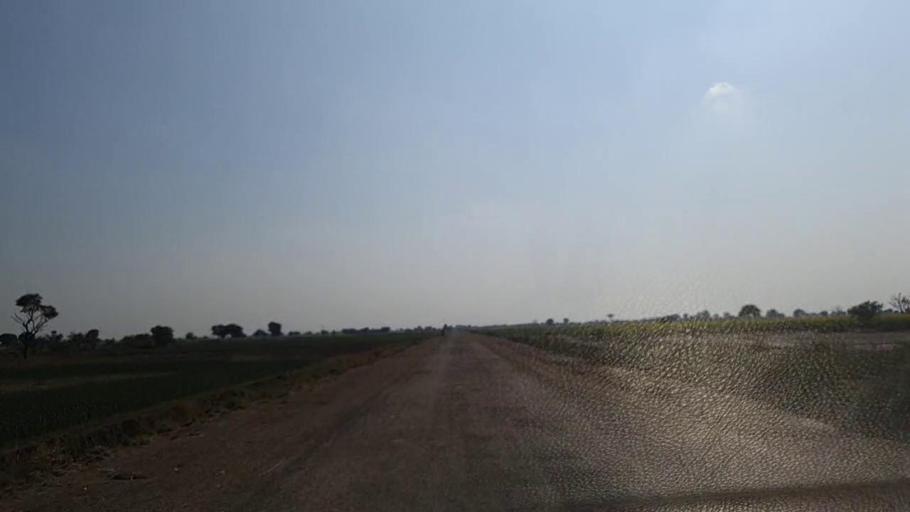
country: PK
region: Sindh
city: Jam Sahib
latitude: 26.2575
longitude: 68.5669
